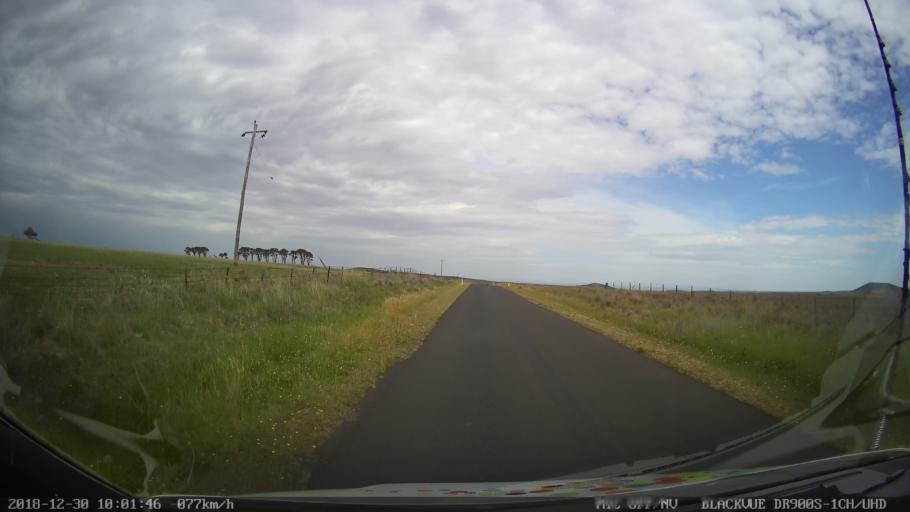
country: AU
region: New South Wales
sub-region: Cooma-Monaro
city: Cooma
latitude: -36.5156
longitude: 149.1810
